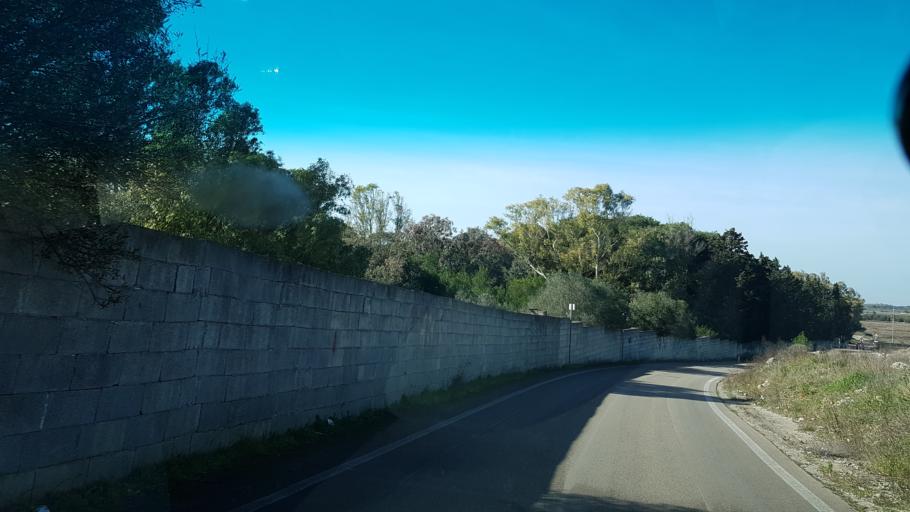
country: IT
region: Apulia
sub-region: Provincia di Lecce
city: Lecce
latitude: 40.3488
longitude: 18.1349
